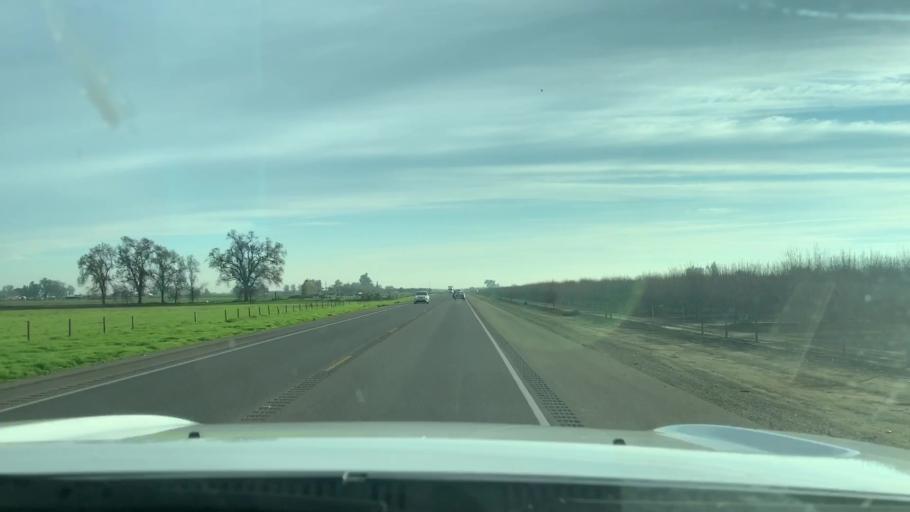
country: US
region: California
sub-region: Fresno County
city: Riverdale
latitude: 36.4222
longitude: -119.8031
